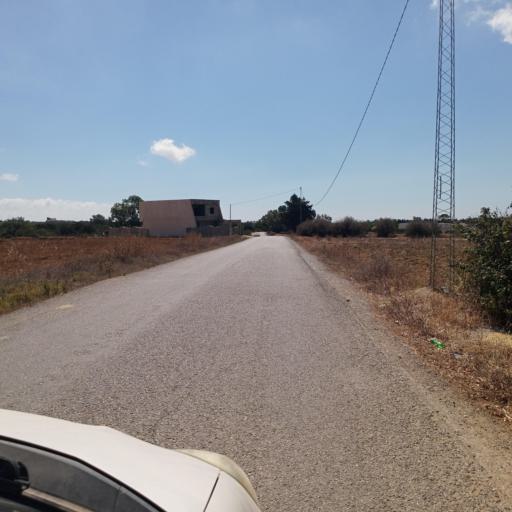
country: TN
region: Nabul
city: Qulaybiyah
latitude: 36.8634
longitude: 11.0369
